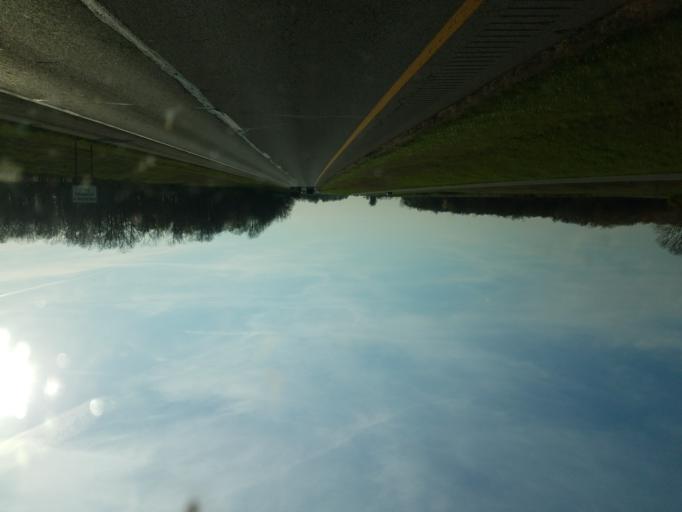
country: US
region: Ohio
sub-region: Clinton County
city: Wilmington
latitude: 39.4806
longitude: -83.9555
